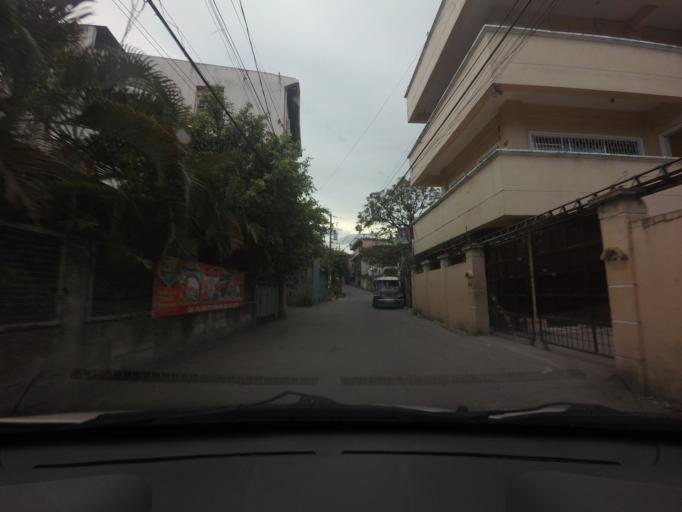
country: PH
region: Calabarzon
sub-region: Province of Rizal
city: Taguig
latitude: 14.5023
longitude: 121.0580
